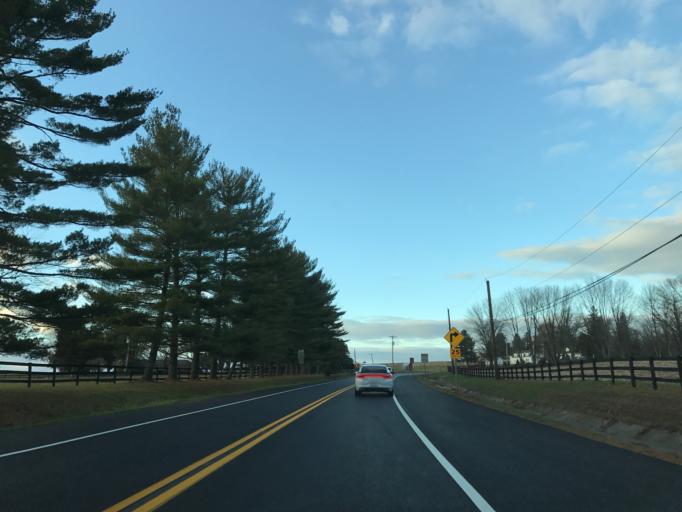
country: US
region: Maryland
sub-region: Harford County
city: Aberdeen
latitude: 39.6333
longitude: -76.2043
